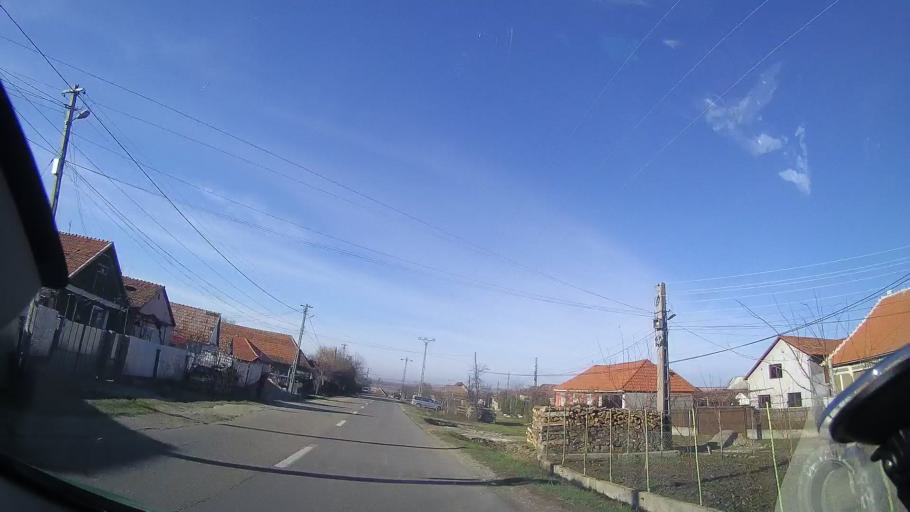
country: RO
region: Bihor
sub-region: Comuna Vadu Crisului
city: Vadu Crisului
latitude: 46.9884
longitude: 22.5276
